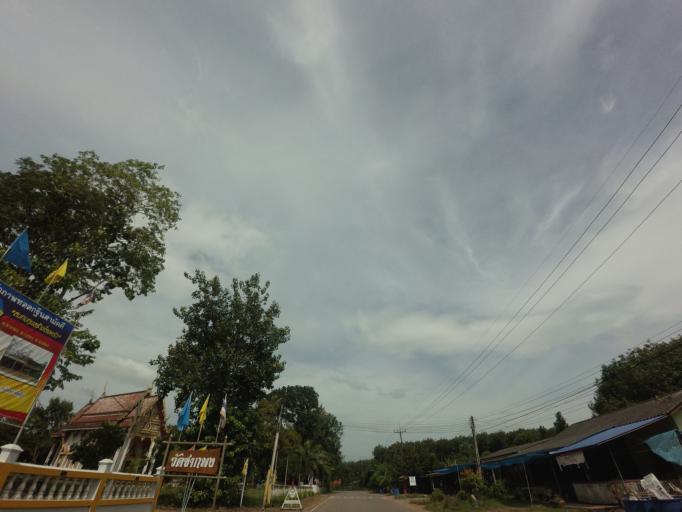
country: TH
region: Rayong
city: Klaeng
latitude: 12.6780
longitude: 101.5528
